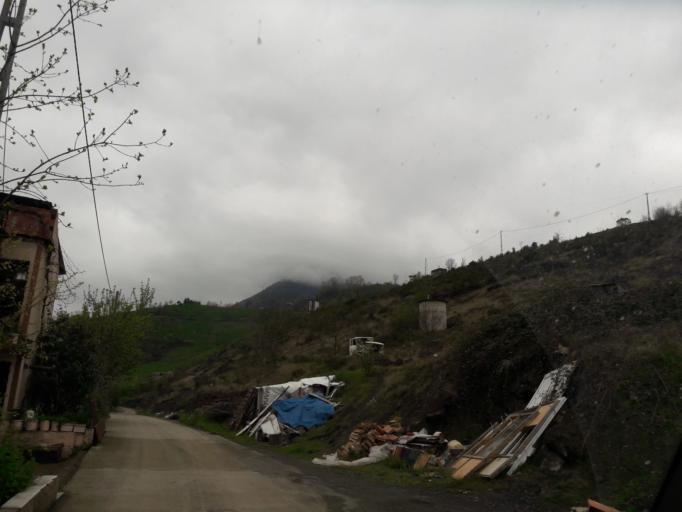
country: TR
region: Trabzon
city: Duzkoy
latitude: 40.9149
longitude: 39.4794
